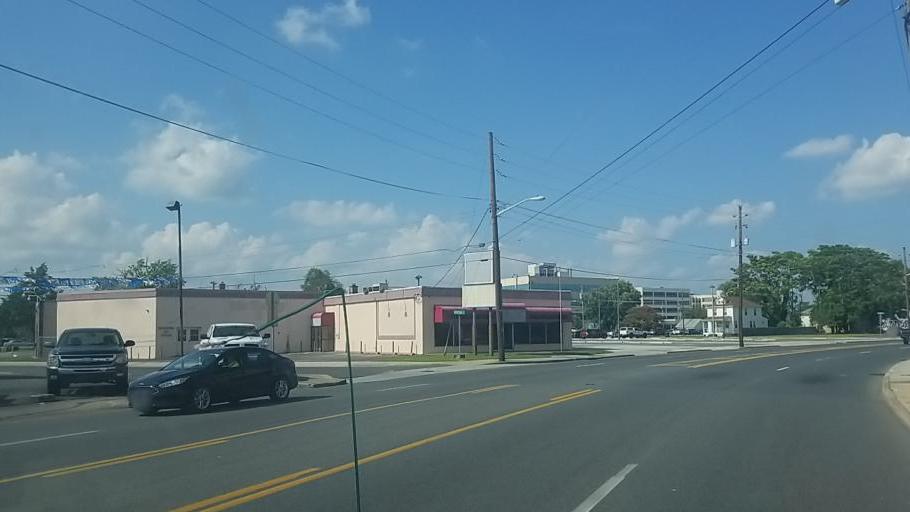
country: US
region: Maryland
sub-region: Wicomico County
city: Salisbury
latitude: 38.3585
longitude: -75.5995
